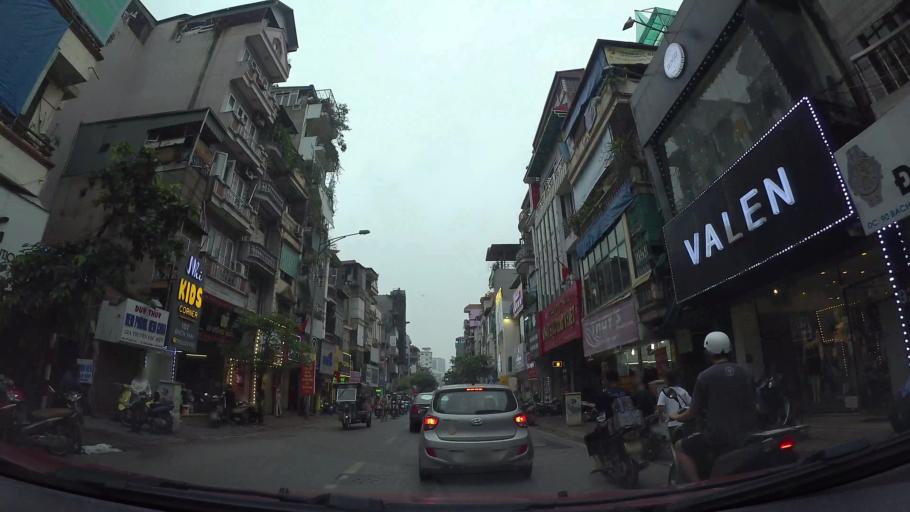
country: VN
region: Ha Noi
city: Hai BaTrung
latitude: 21.0068
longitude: 105.8513
